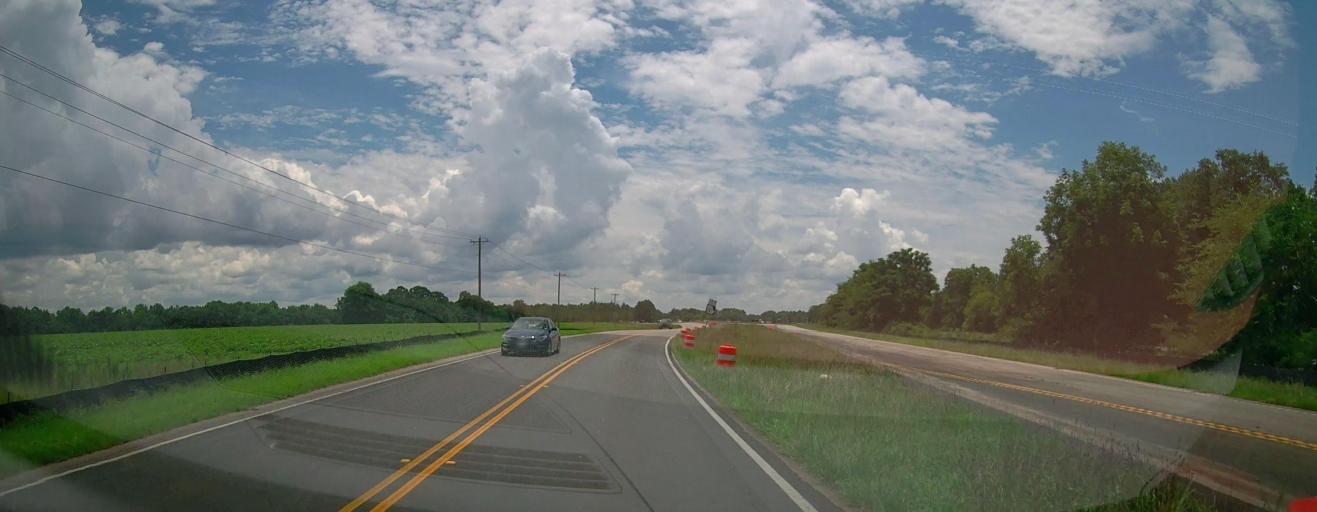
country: US
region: Georgia
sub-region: Houston County
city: Perry
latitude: 32.4710
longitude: -83.6149
